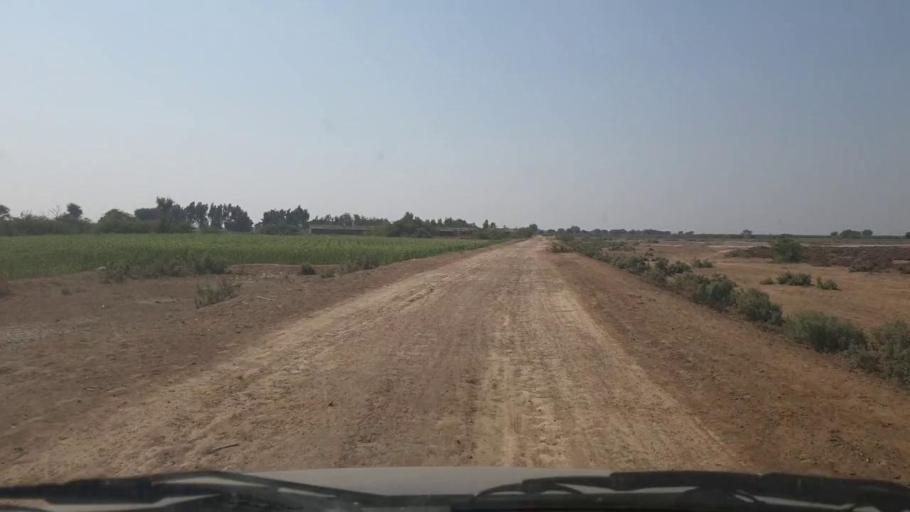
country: PK
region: Sindh
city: Samaro
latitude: 25.2647
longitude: 69.3414
